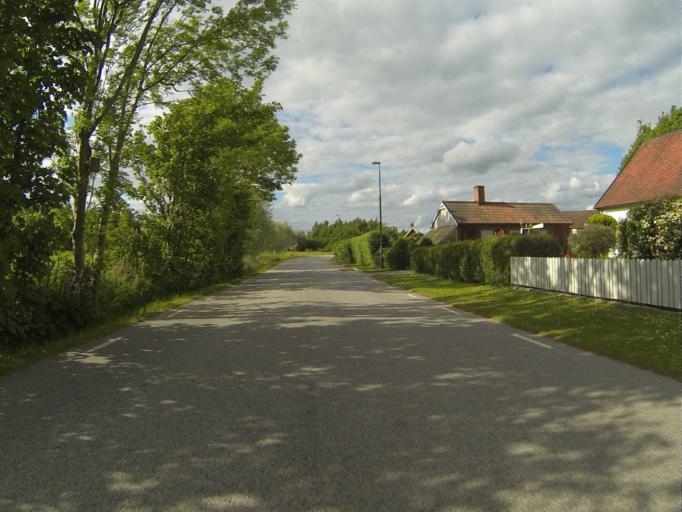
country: SE
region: Skane
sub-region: Staffanstorps Kommun
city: Staffanstorp
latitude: 55.6331
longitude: 13.2268
